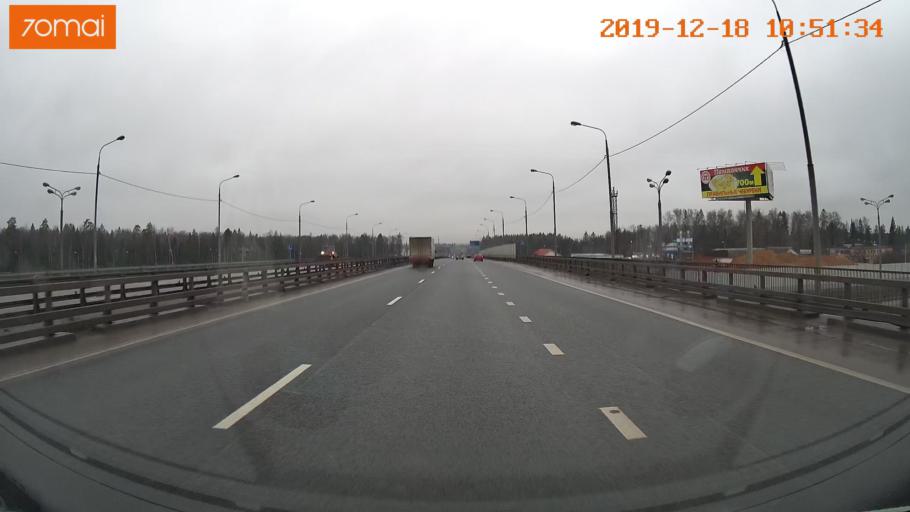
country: RU
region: Moskovskaya
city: Selyatino
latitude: 55.5157
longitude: 36.9971
